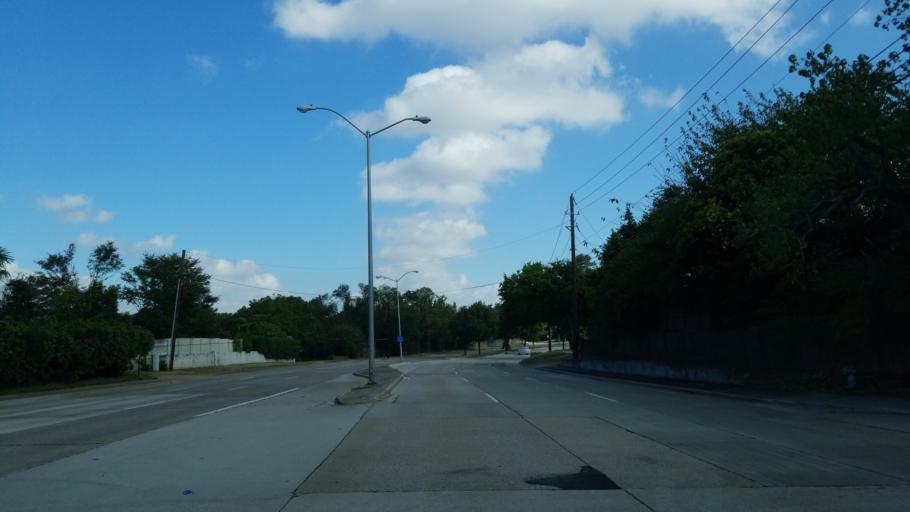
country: US
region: Texas
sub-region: Dallas County
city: Addison
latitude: 32.9476
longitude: -96.7856
